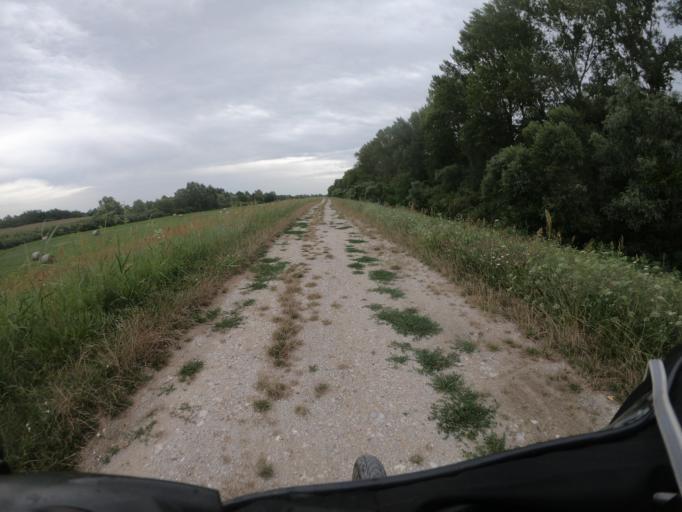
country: HU
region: Jasz-Nagykun-Szolnok
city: Tiszafured
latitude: 47.6854
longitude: 20.7894
